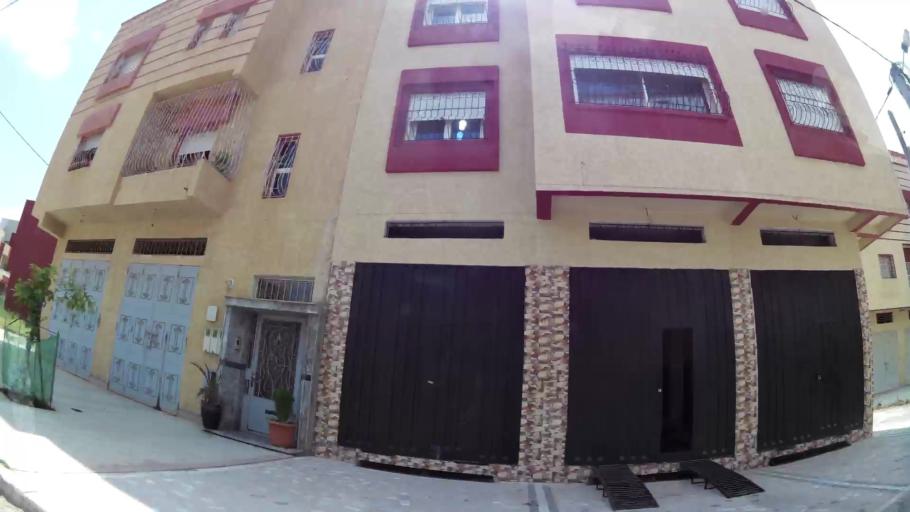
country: MA
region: Gharb-Chrarda-Beni Hssen
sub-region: Kenitra Province
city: Kenitra
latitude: 34.0105
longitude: -6.5359
